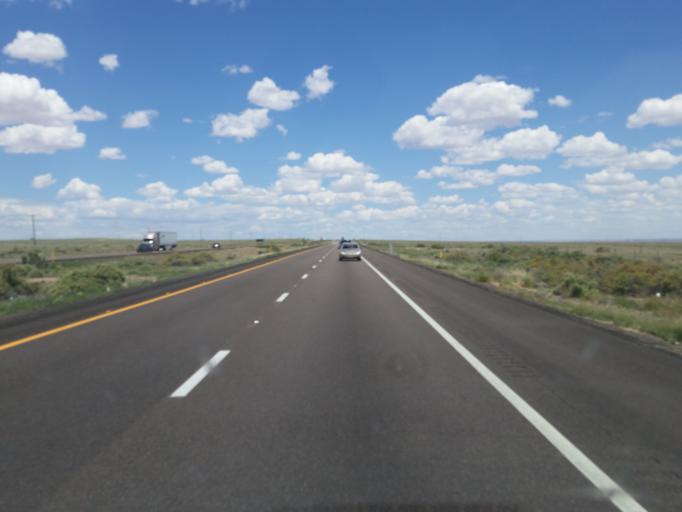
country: US
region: Arizona
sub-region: Navajo County
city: Holbrook
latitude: 34.9851
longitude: -110.0289
